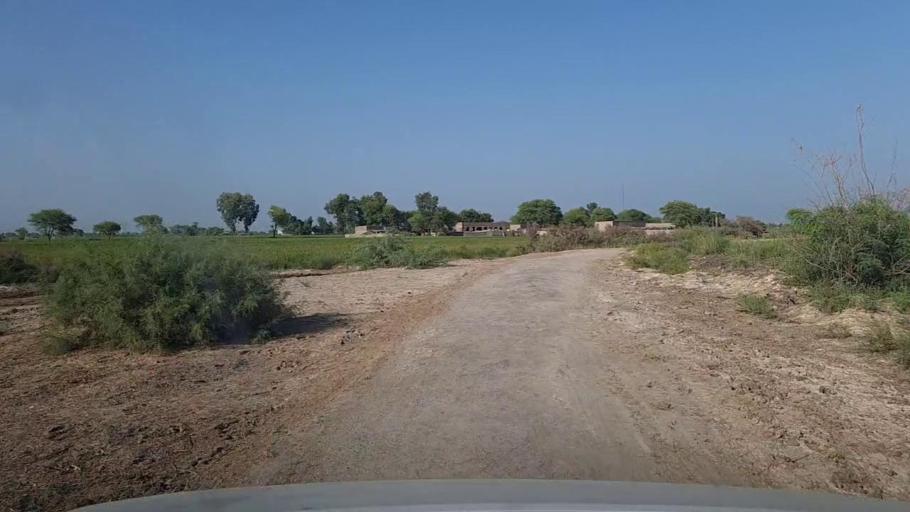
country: PK
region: Sindh
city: Kandhkot
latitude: 28.2787
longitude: 69.3184
